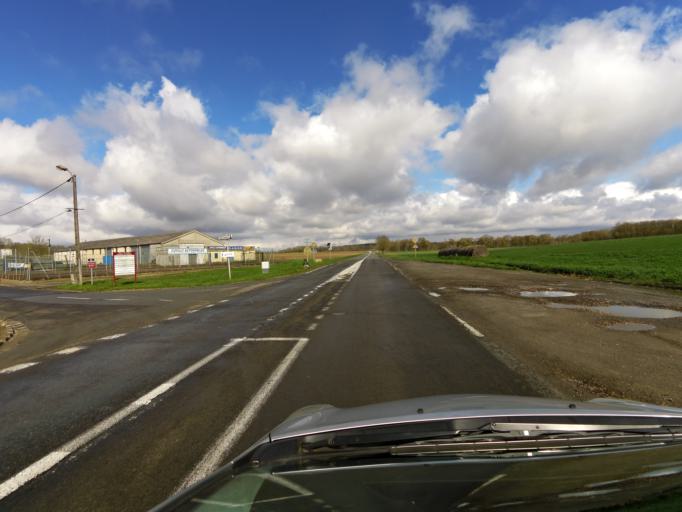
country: FR
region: Picardie
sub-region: Departement de l'Oise
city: Ressons-sur-Matz
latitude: 49.5565
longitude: 2.7002
